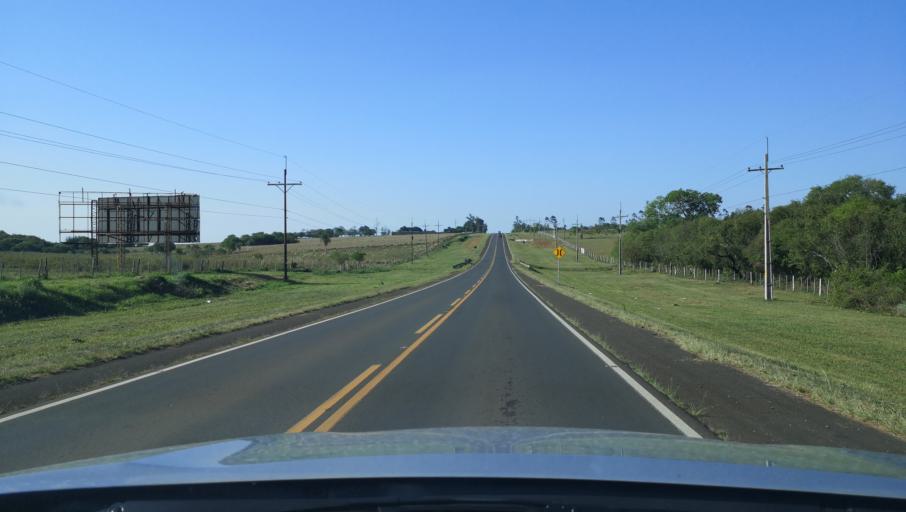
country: PY
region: Misiones
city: Santa Maria
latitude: -26.8313
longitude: -57.0315
